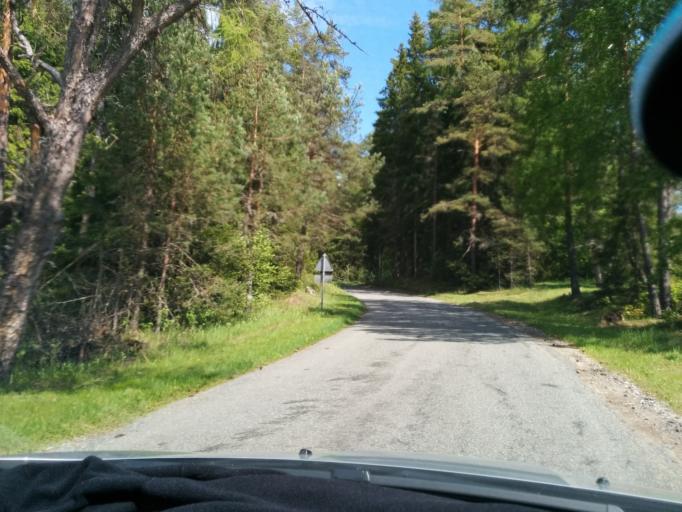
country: EE
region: Laeaene-Virumaa
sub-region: Kadrina vald
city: Kadrina
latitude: 59.5164
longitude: 25.9769
